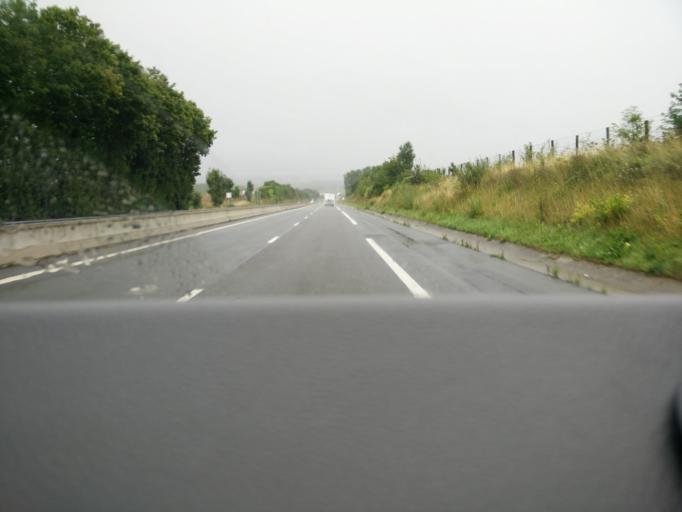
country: FR
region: Nord-Pas-de-Calais
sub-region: Departement du Pas-de-Calais
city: Marconnelle
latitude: 50.3624
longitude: 2.0091
